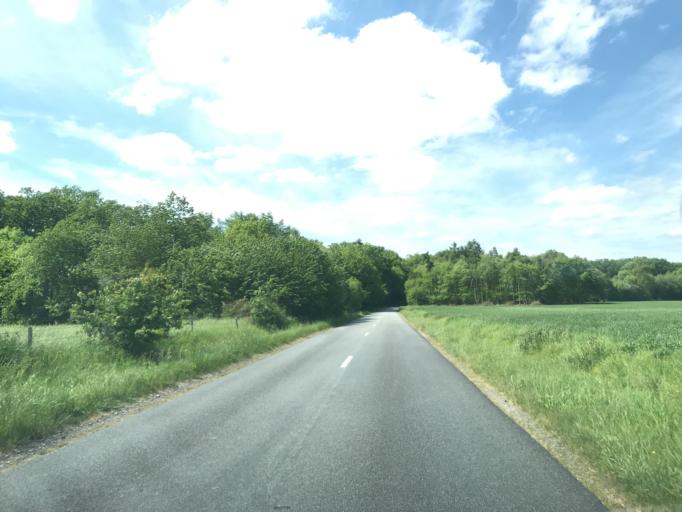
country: FR
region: Haute-Normandie
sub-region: Departement de l'Eure
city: Beaumont-le-Roger
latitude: 49.1503
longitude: 0.8214
